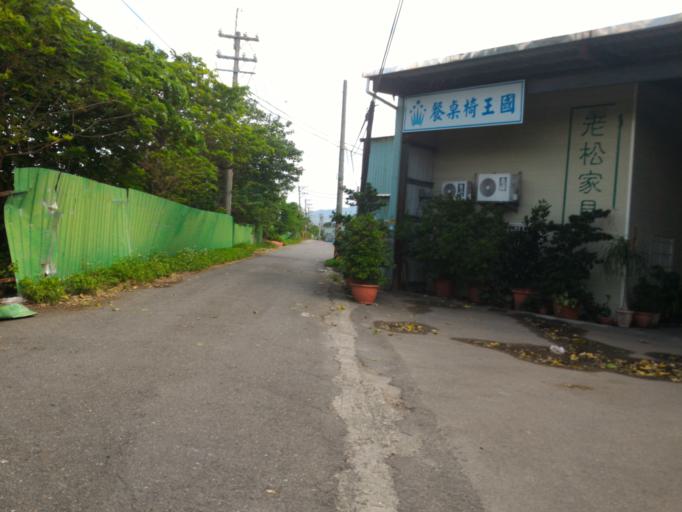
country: TW
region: Taipei
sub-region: Taipei
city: Banqiao
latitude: 24.9644
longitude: 121.4004
